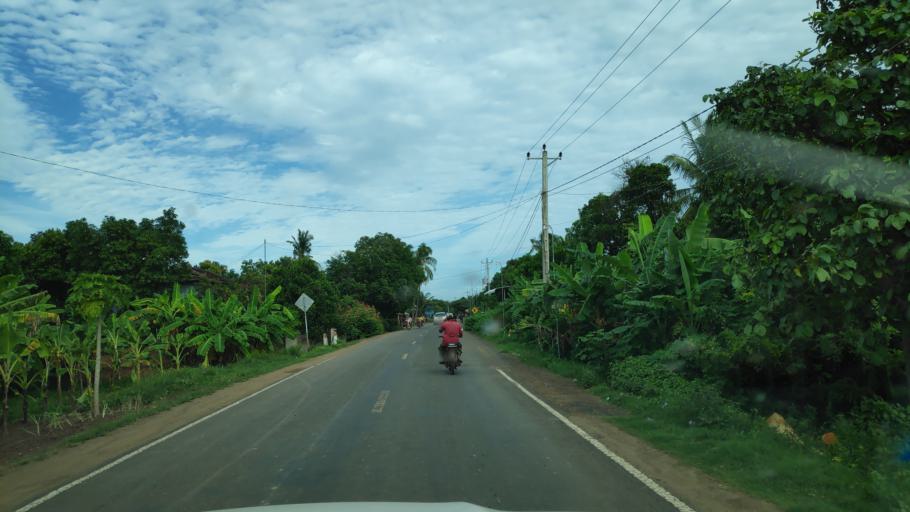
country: KH
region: Kampong Cham
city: Kampong Cham
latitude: 11.9471
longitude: 105.2433
